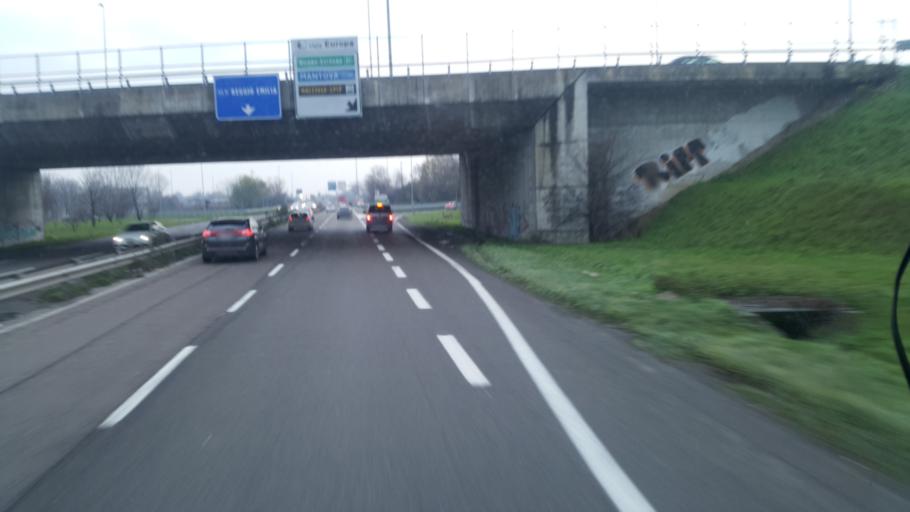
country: IT
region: Emilia-Romagna
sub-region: Provincia di Parma
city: Parma
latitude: 44.8217
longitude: 10.3266
